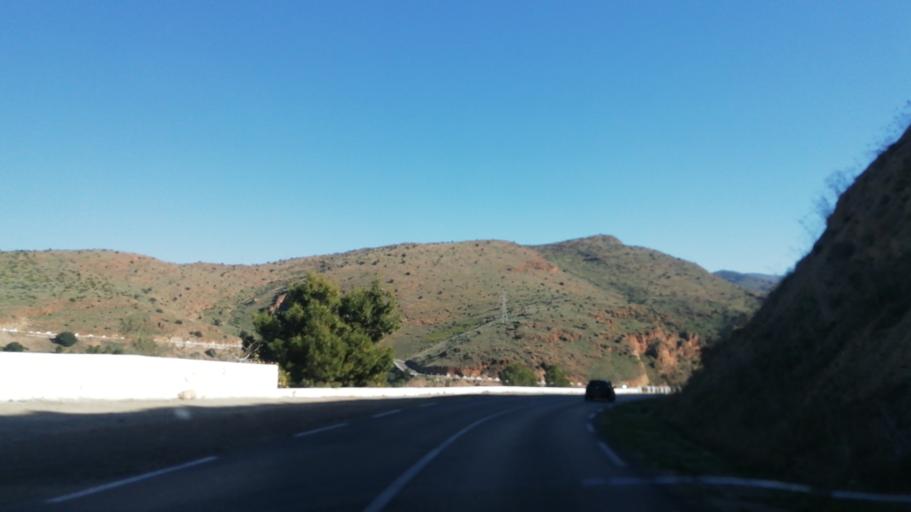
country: DZ
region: Tlemcen
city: Beni Mester
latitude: 34.8410
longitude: -1.4693
